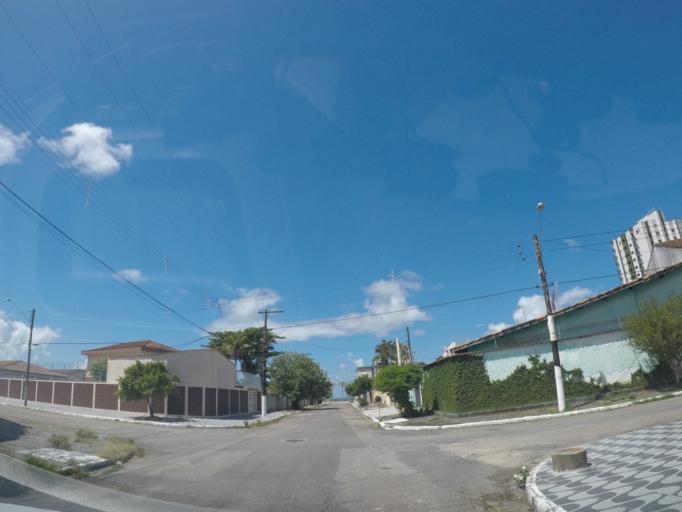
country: BR
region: Sao Paulo
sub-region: Mongagua
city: Mongagua
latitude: -24.0765
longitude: -46.5838
